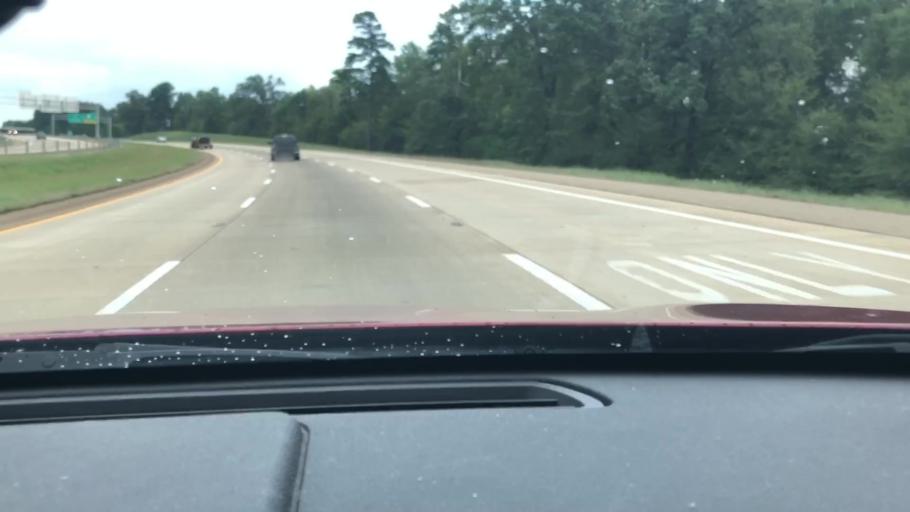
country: US
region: Texas
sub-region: Bowie County
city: Texarkana
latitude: 33.4038
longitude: -94.0053
